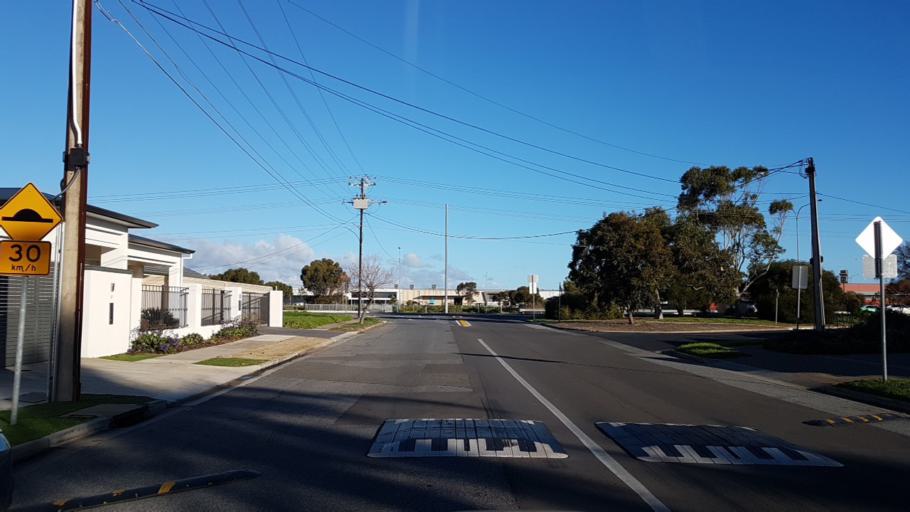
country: AU
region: South Australia
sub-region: City of West Torrens
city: Plympton
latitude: -34.9332
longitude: 138.5241
